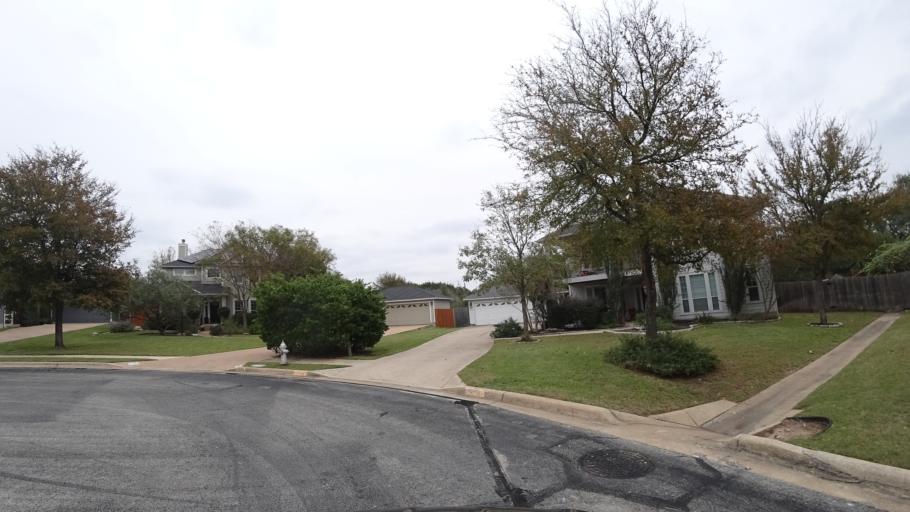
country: US
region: Texas
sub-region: Travis County
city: Shady Hollow
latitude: 30.2035
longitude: -97.8814
